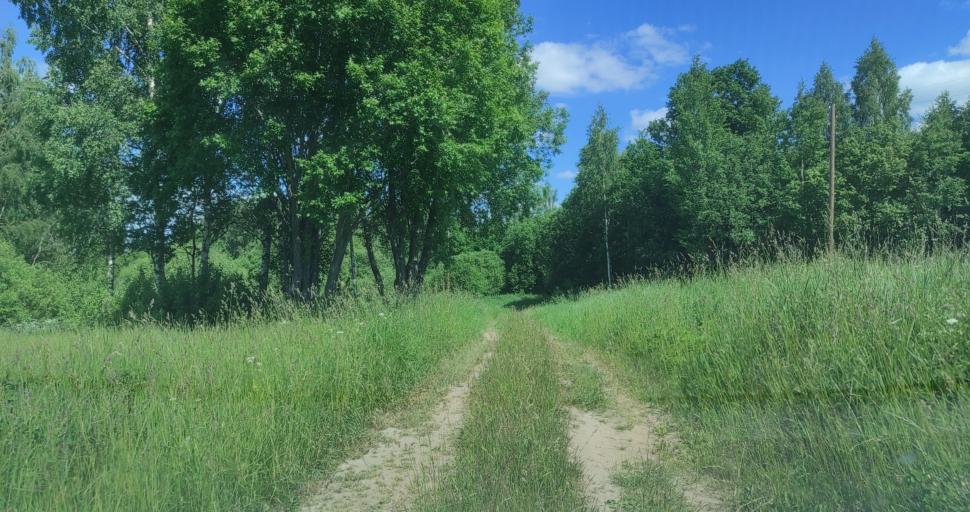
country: LV
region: Aizpute
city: Aizpute
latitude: 56.8609
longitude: 21.7292
